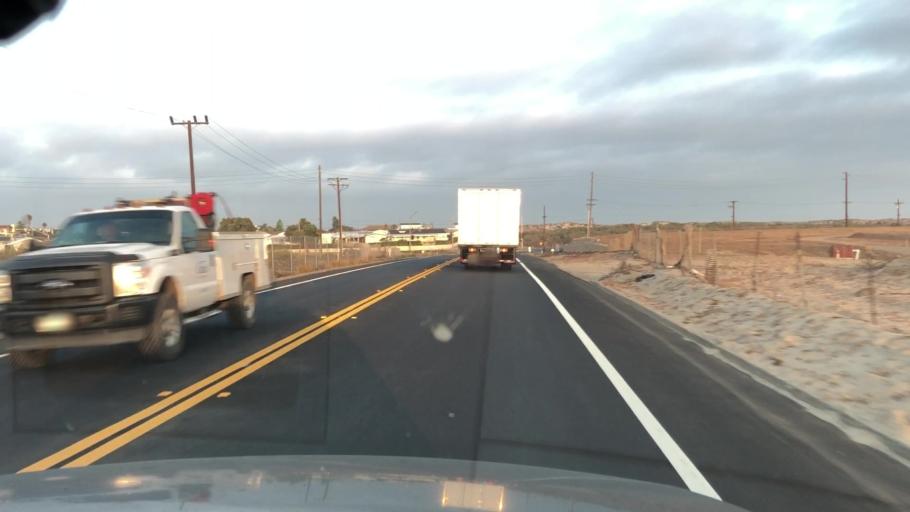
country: US
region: California
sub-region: Ventura County
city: Oxnard Shores
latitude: 34.1978
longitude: -119.2401
